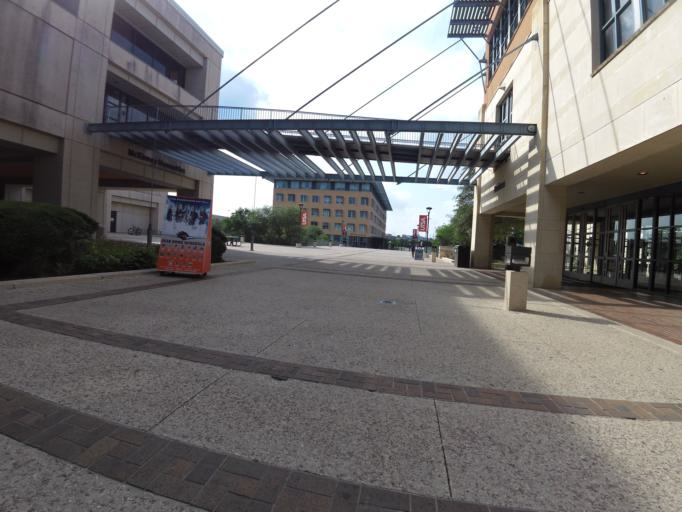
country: US
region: Texas
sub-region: Bexar County
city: Shavano Park
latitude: 29.5847
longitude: -98.6185
